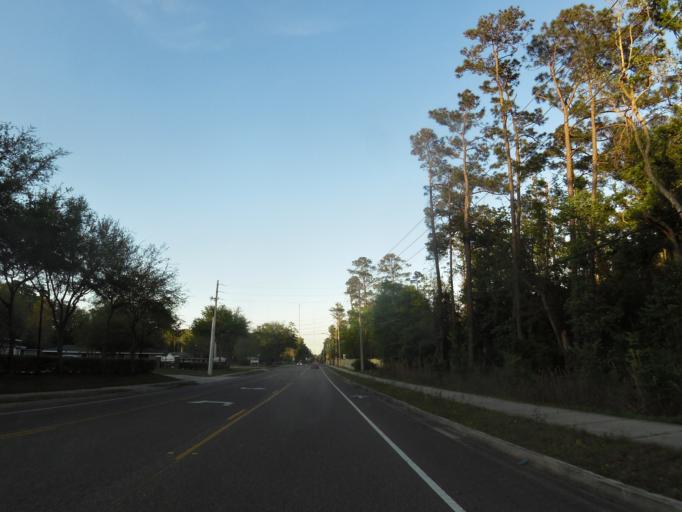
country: US
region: Florida
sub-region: Duval County
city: Jacksonville
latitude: 30.2582
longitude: -81.5804
